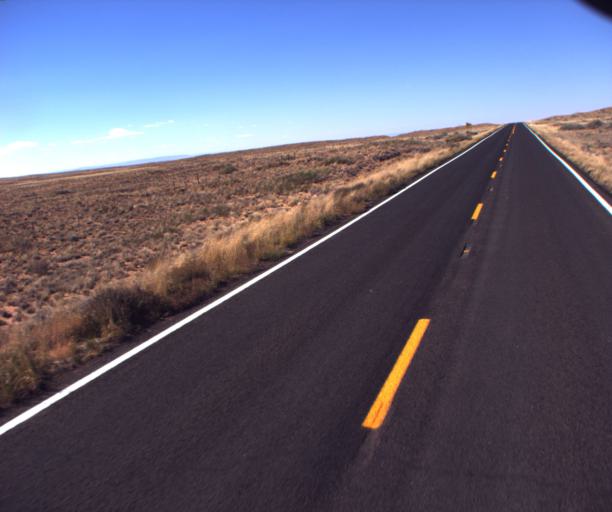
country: US
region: Arizona
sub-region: Coconino County
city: Tuba City
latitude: 35.9682
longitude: -110.9571
